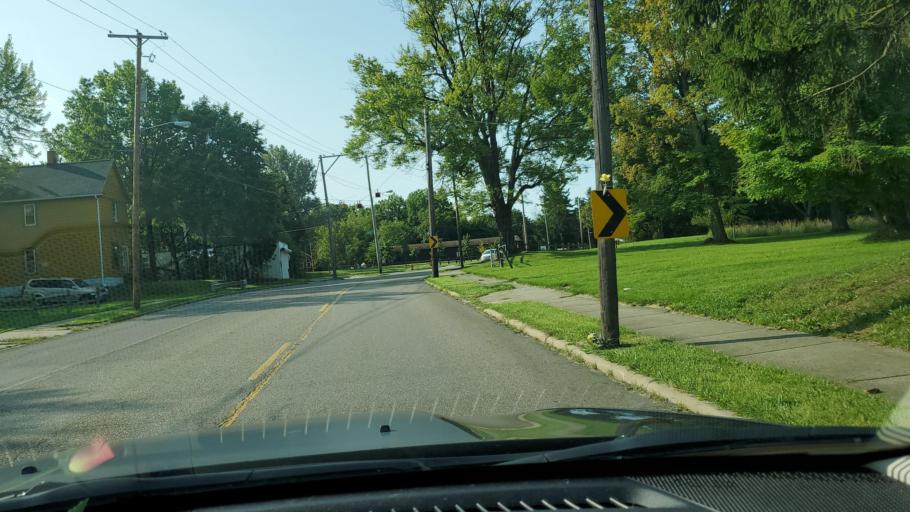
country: US
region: Ohio
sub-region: Mahoning County
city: Youngstown
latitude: 41.0894
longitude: -80.6713
